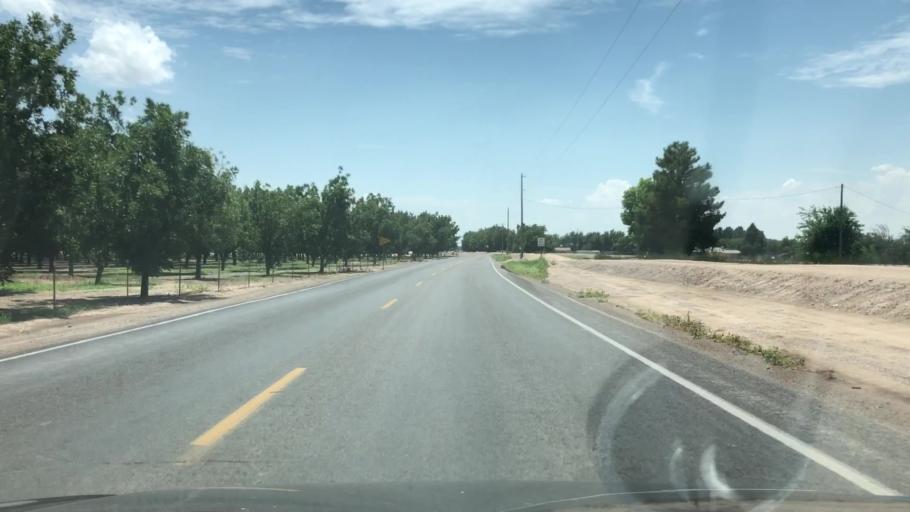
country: US
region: New Mexico
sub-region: Dona Ana County
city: La Union
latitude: 32.0083
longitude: -106.6638
